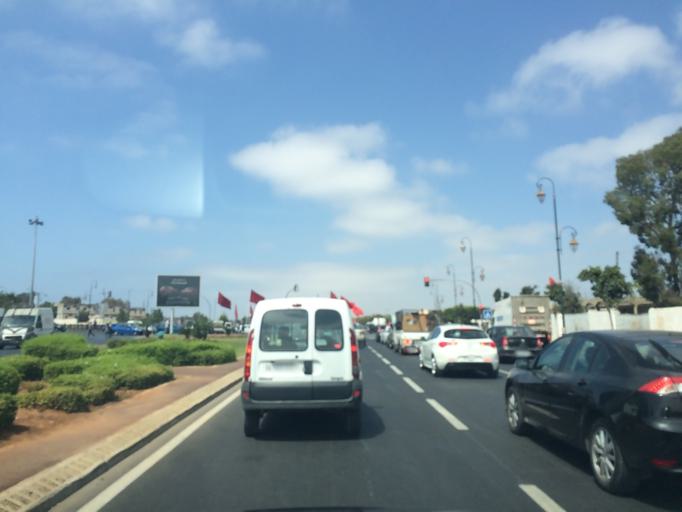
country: MA
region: Rabat-Sale-Zemmour-Zaer
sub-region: Rabat
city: Rabat
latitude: 33.9903
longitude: -6.8666
